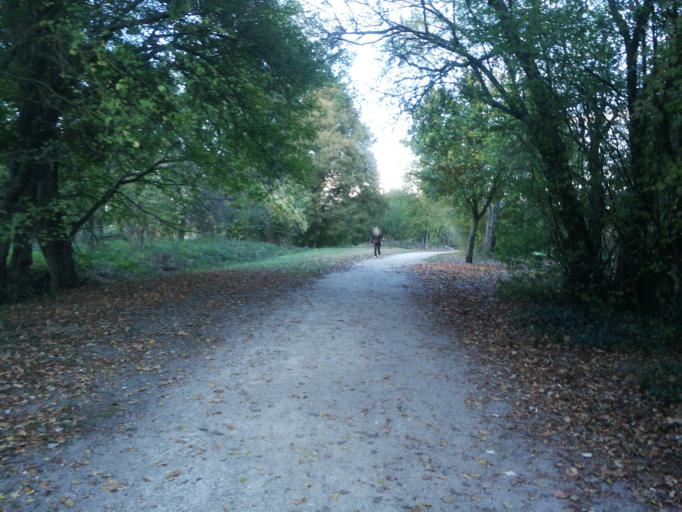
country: FR
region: Centre
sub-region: Departement d'Indre-et-Loire
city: Chanceaux-sur-Choisille
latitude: 47.4404
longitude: 0.6882
